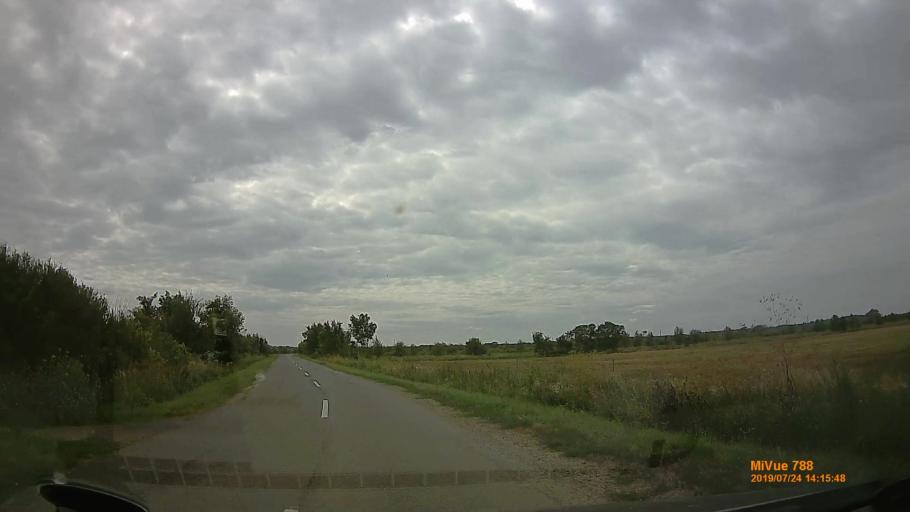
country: UA
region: Zakarpattia
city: Batiovo
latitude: 48.3203
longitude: 22.3023
